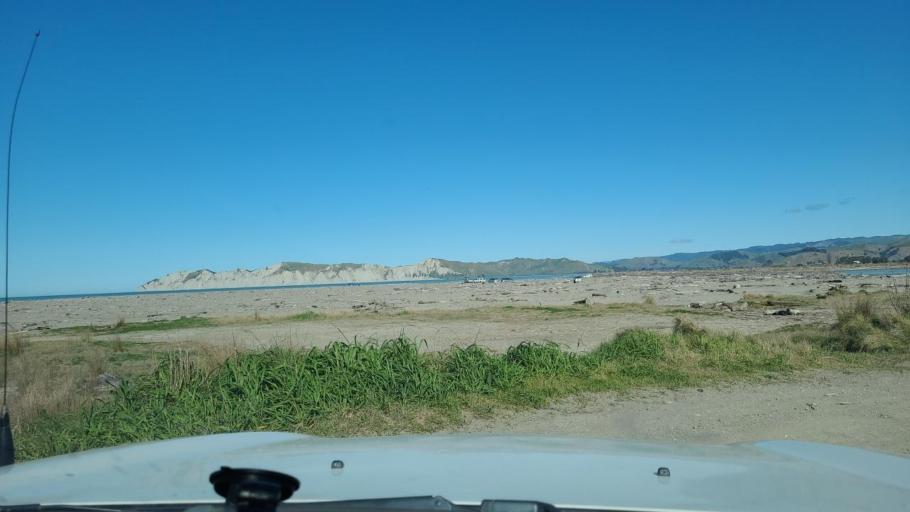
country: NZ
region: Gisborne
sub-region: Gisborne District
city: Gisborne
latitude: -38.7096
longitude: 177.9428
